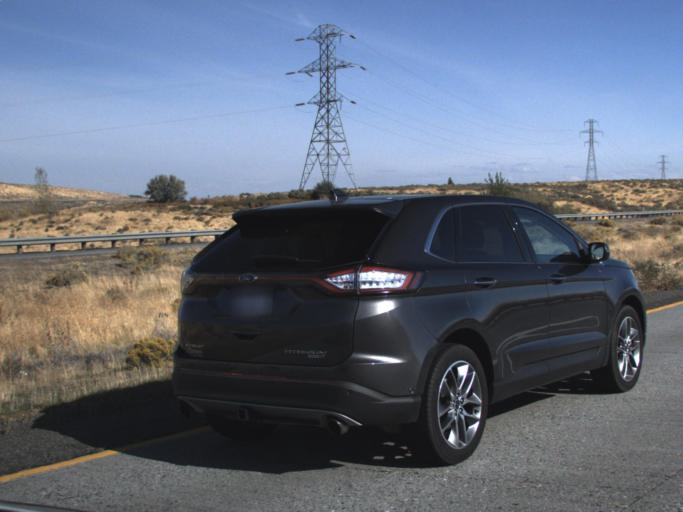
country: US
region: Washington
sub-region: Franklin County
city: West Pasco
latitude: 46.1778
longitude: -119.2349
